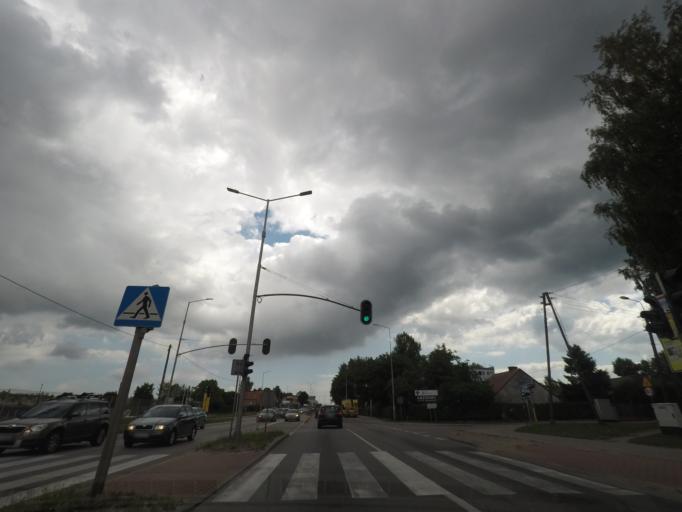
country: PL
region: Pomeranian Voivodeship
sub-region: Powiat wejherowski
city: Rumia
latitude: 54.5625
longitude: 18.3956
